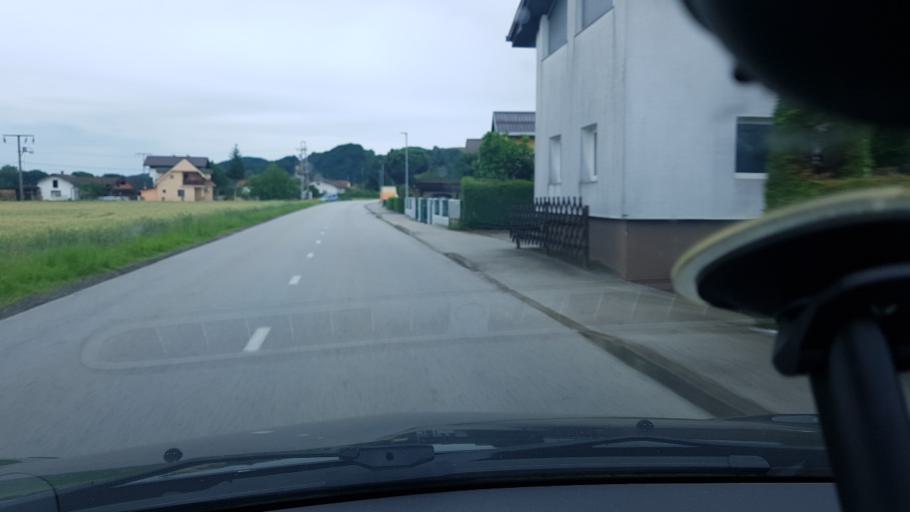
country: SI
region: Videm
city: Videm pri Ptuju
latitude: 46.3727
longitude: 15.8924
